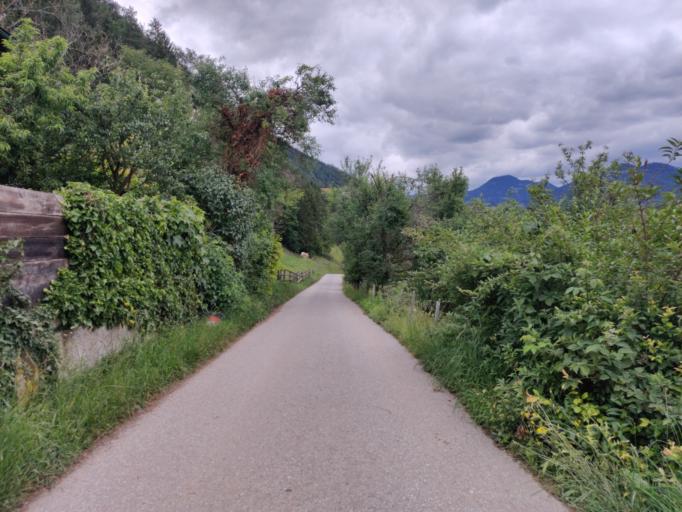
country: AT
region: Styria
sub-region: Politischer Bezirk Graz-Umgebung
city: Frohnleiten
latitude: 47.2412
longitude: 15.3096
